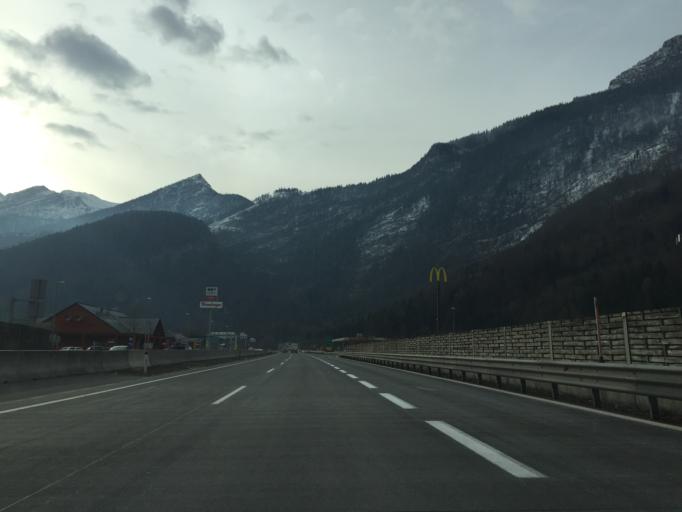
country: AT
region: Salzburg
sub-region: Politischer Bezirk Hallein
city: Golling an der Salzach
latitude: 47.5855
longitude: 13.1559
